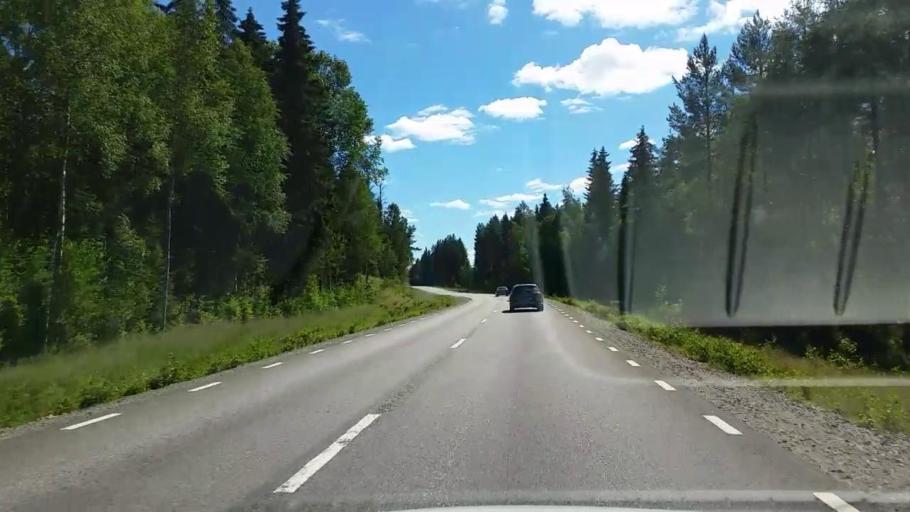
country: SE
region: Gaevleborg
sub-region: Ovanakers Kommun
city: Edsbyn
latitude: 61.1964
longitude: 15.8738
